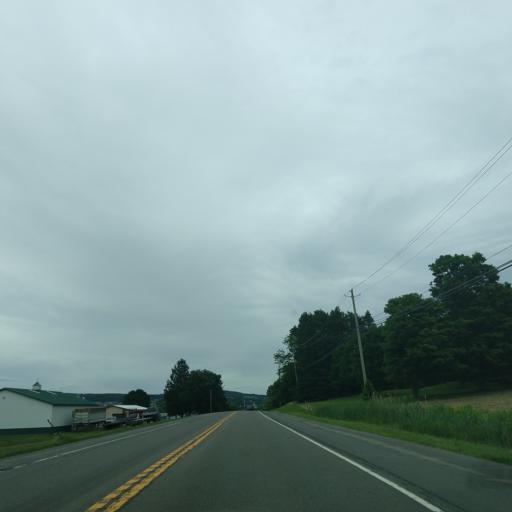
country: US
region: New York
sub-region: Tompkins County
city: Dryden
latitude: 42.4899
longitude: -76.3200
